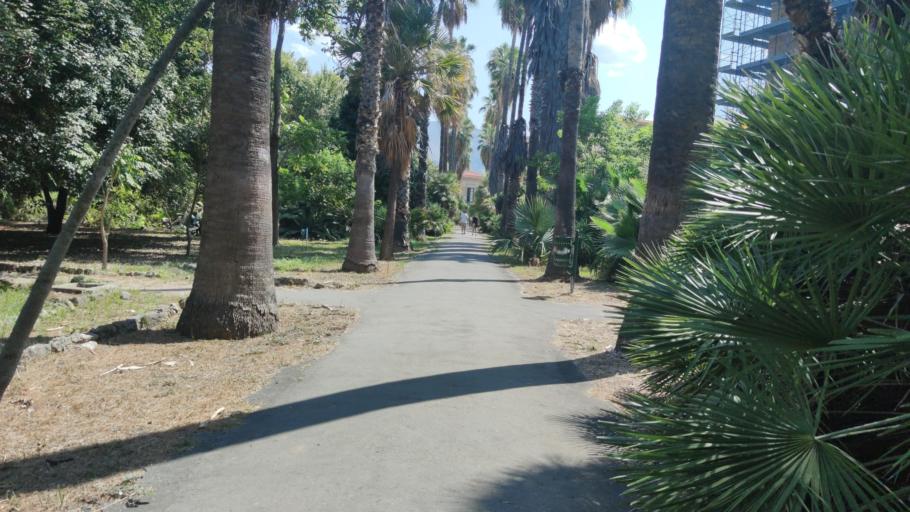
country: IT
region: Sicily
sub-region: Palermo
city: Palermo
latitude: 38.1105
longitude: 13.3738
